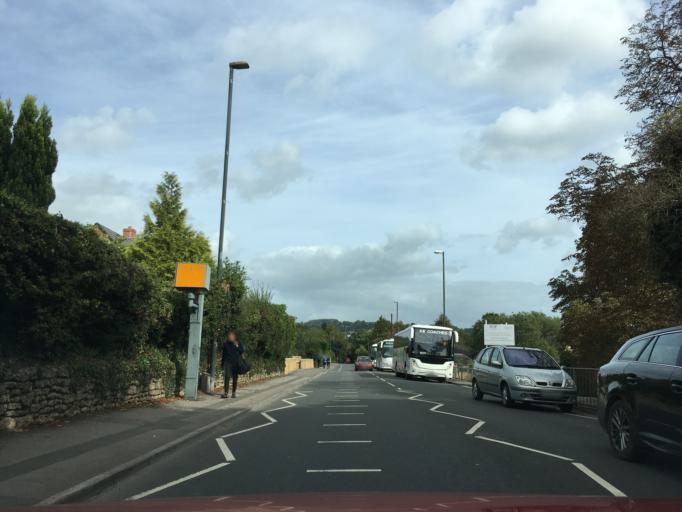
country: GB
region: England
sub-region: Gloucestershire
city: Stroud
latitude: 51.7450
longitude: -2.2309
